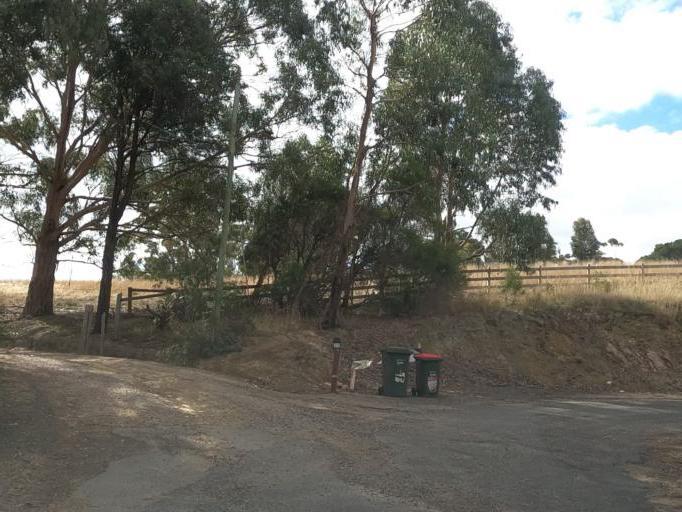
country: AU
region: Victoria
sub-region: Hume
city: Greenvale
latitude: -37.5559
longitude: 144.8631
